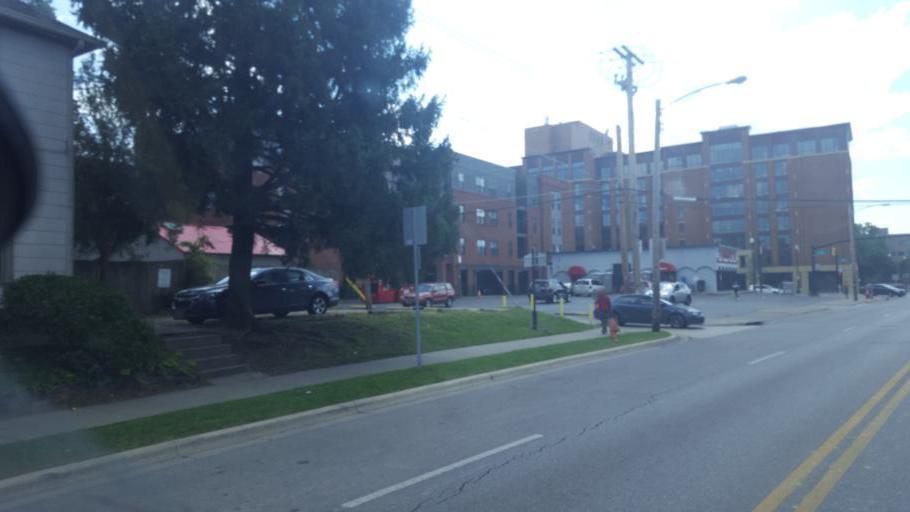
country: US
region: Ohio
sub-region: Franklin County
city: Grandview Heights
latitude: 40.0071
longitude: -83.0142
